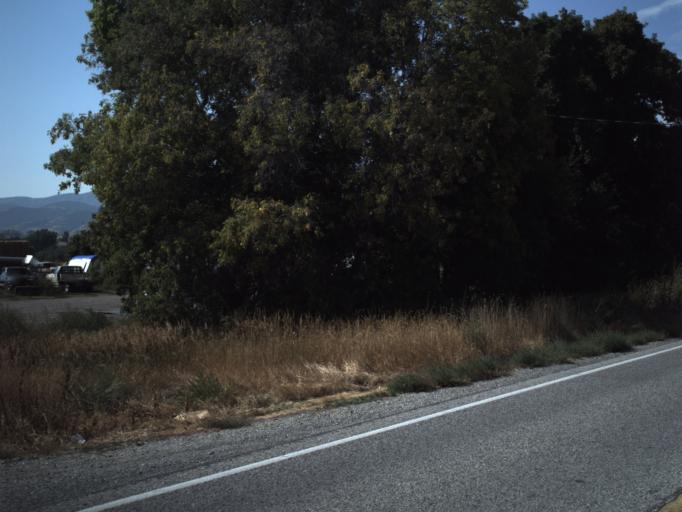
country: US
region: Utah
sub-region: Cache County
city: Hyrum
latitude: 41.6410
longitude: -111.8839
